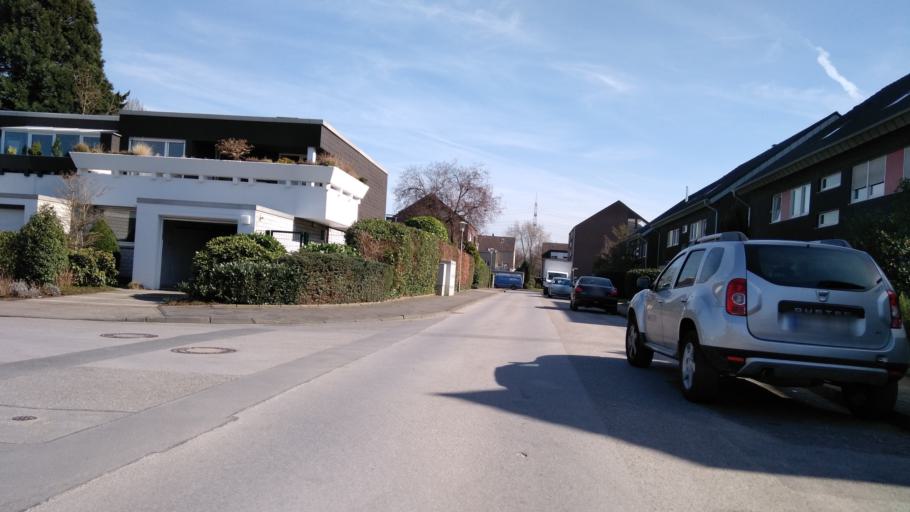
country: DE
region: North Rhine-Westphalia
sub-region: Regierungsbezirk Munster
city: Gladbeck
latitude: 51.5974
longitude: 6.9312
